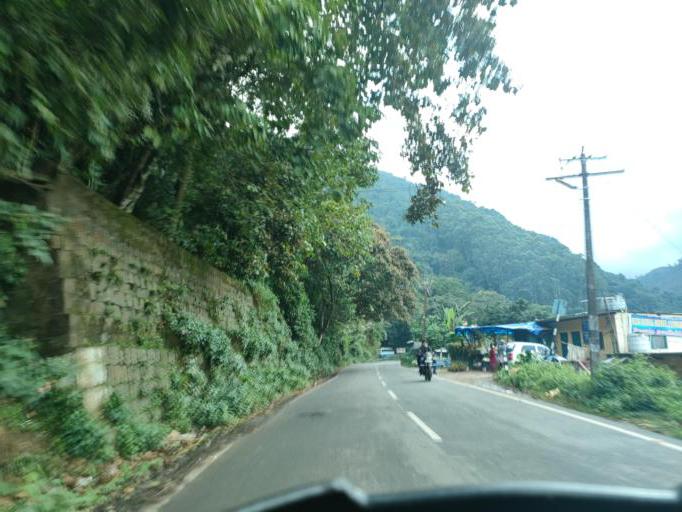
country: IN
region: Tamil Nadu
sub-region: Dindigul
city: Kodaikanal
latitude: 10.2574
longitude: 77.5316
